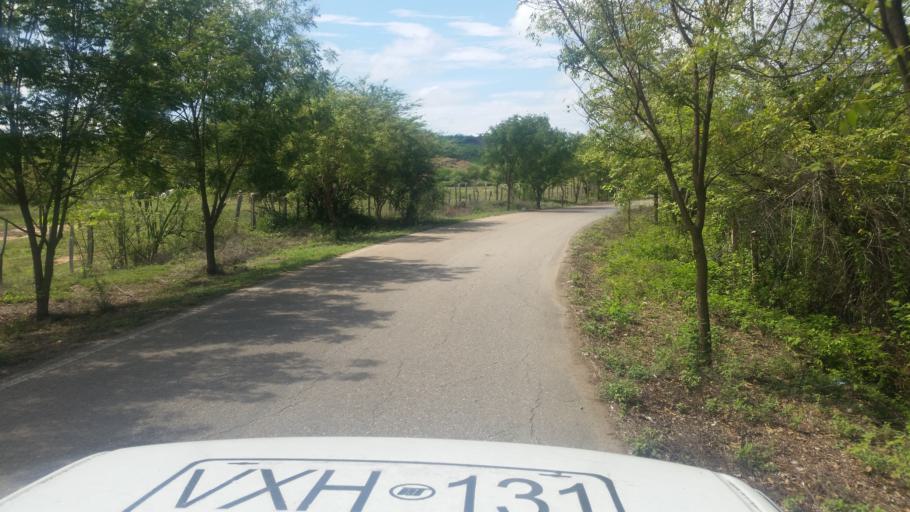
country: CO
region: Huila
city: Villavieja
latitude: 3.2020
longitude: -75.2095
